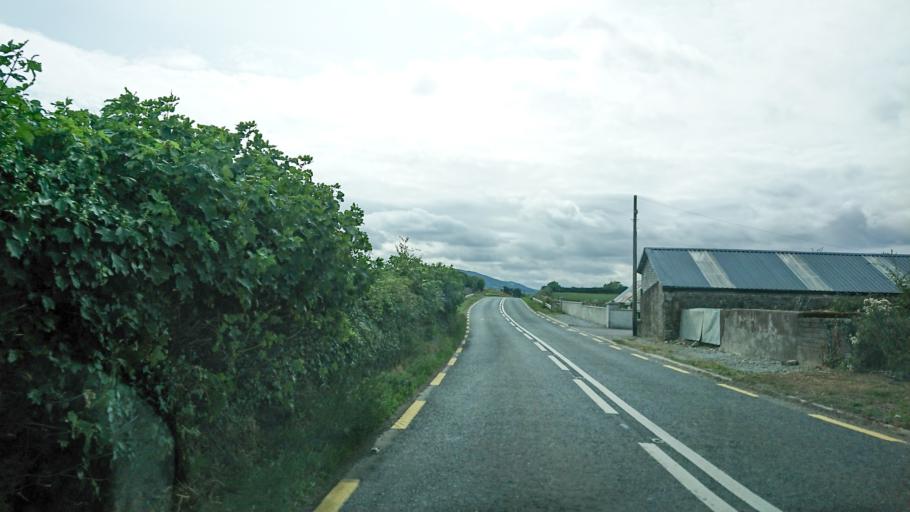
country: IE
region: Munster
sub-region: County Cork
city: Mallow
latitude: 52.1575
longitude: -8.4894
